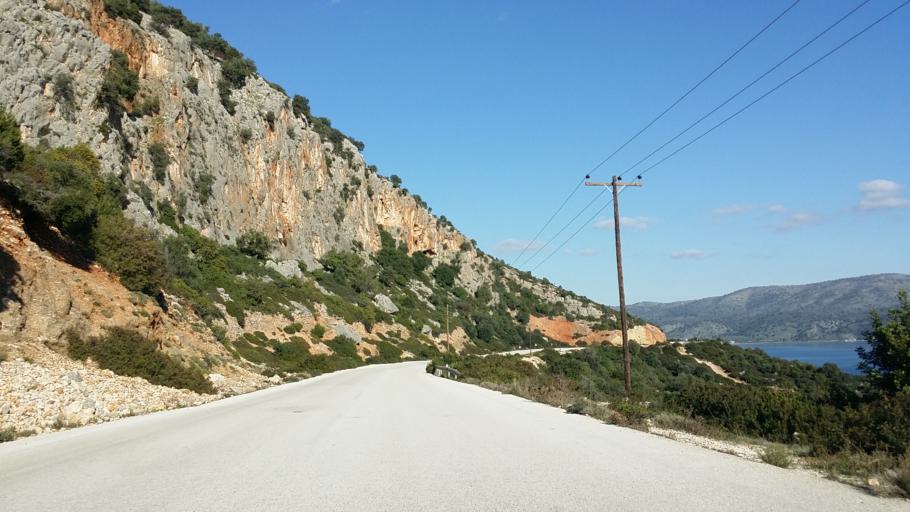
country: GR
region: West Greece
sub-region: Nomos Aitolias kai Akarnanias
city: Astakos
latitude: 38.5125
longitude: 21.0496
